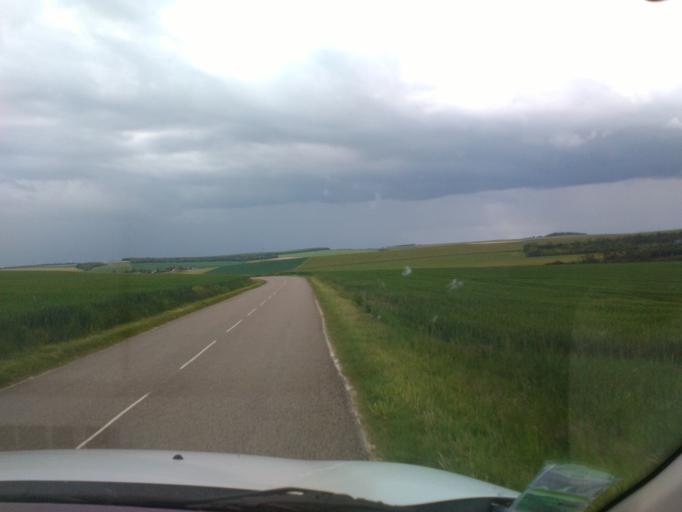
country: FR
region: Bourgogne
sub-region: Departement de l'Yonne
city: Thorigny-sur-Oreuse
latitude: 48.3593
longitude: 3.4353
